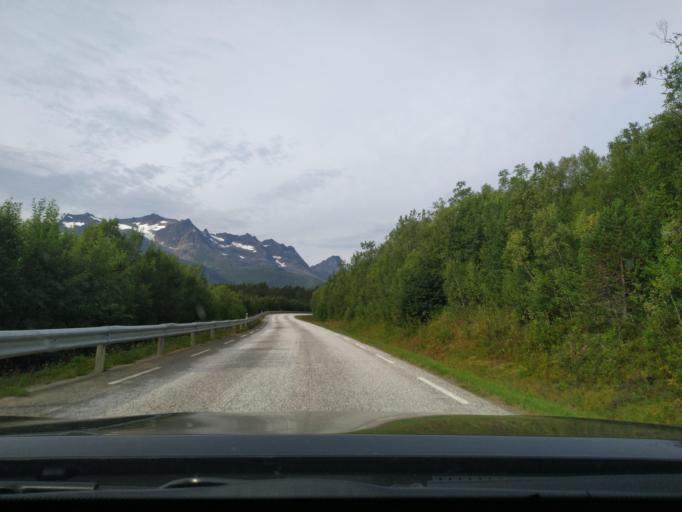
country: NO
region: Troms
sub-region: Dyroy
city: Brostadbotn
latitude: 68.9110
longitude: 17.5359
